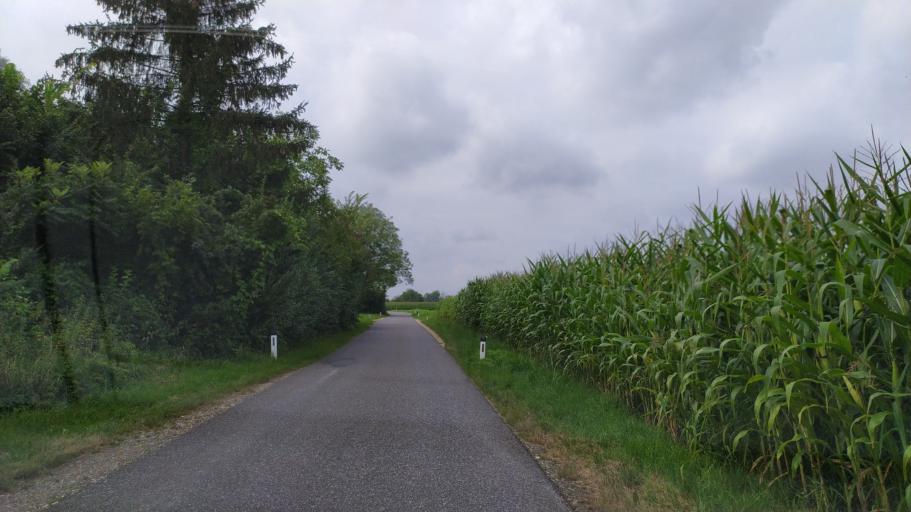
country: AT
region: Upper Austria
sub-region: Politischer Bezirk Perg
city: Bad Kreuzen
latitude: 48.1955
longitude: 14.7726
